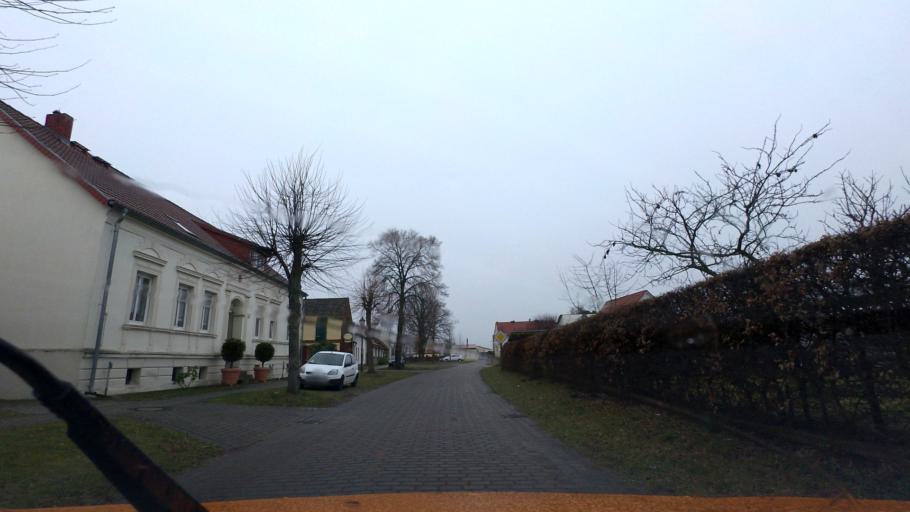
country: DE
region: Brandenburg
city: Brieselang
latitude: 52.6547
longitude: 12.9779
